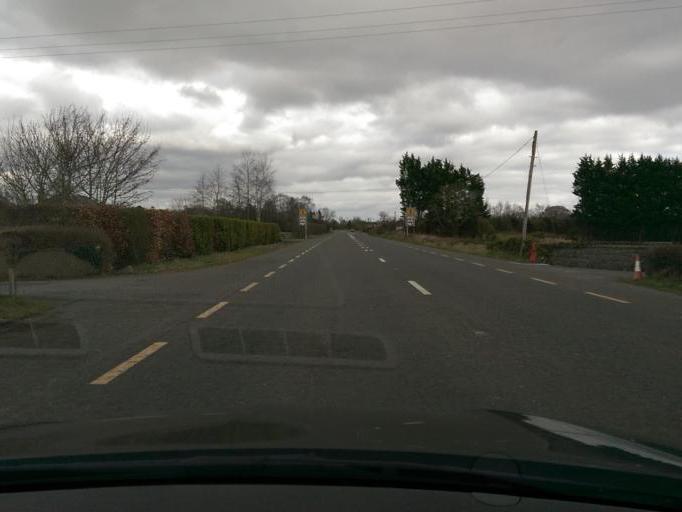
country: IE
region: Leinster
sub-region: An Iarmhi
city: Athlone
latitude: 53.3687
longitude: -8.0315
